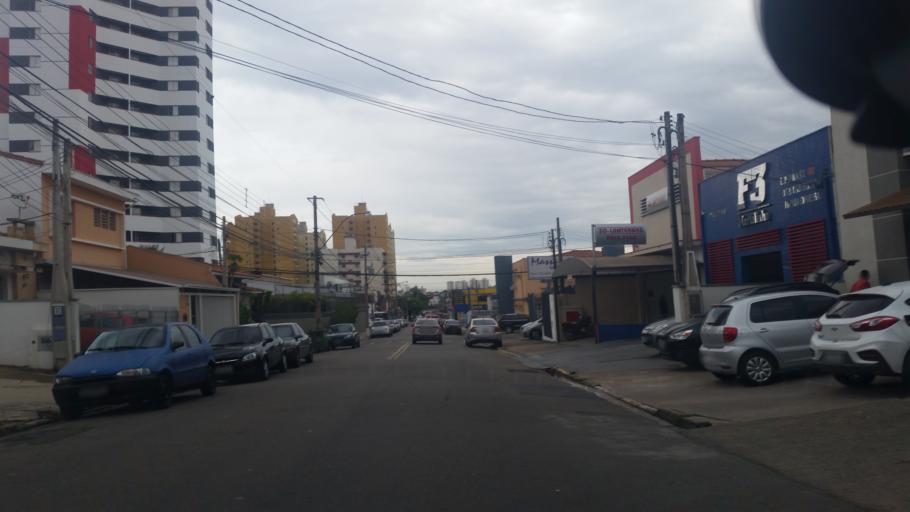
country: BR
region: Sao Paulo
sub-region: Campinas
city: Campinas
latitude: -22.8846
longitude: -47.0604
